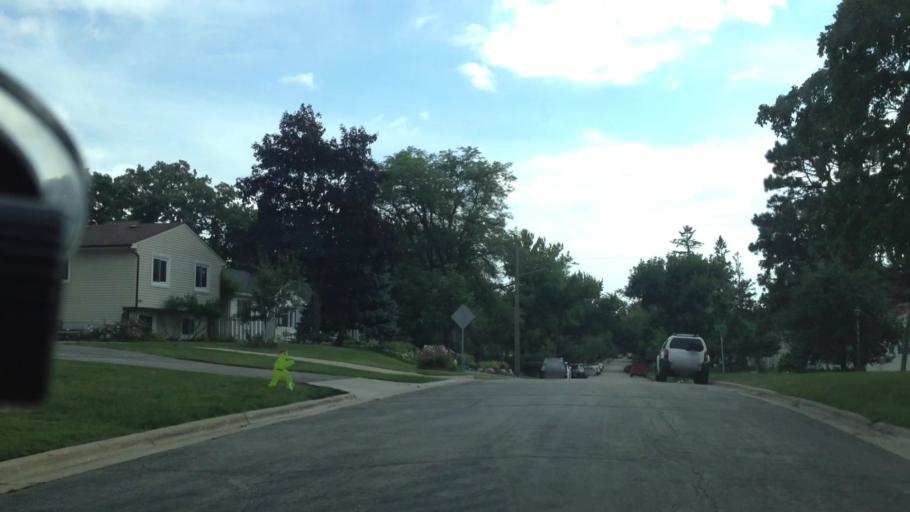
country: US
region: Minnesota
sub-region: Hennepin County
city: Saint Louis Park
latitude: 44.9520
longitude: -93.3545
